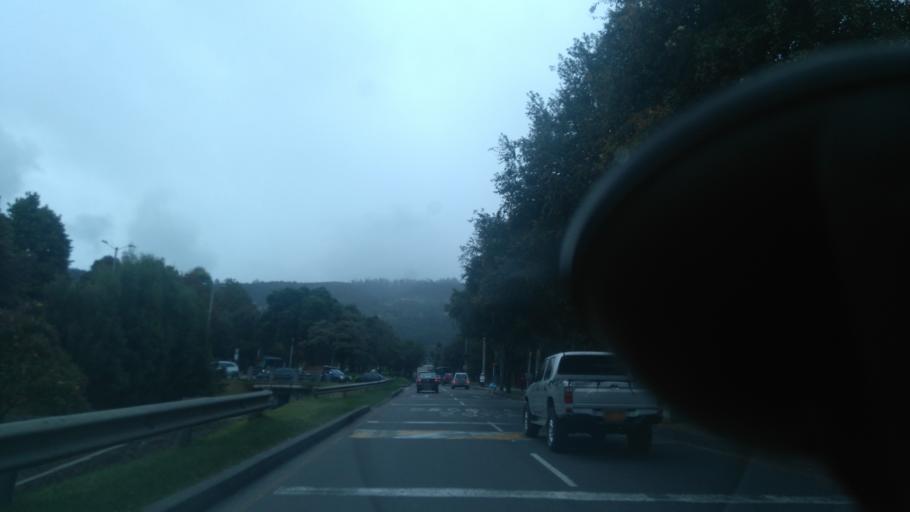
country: CO
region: Cundinamarca
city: La Calera
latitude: 4.7484
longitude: -74.0339
